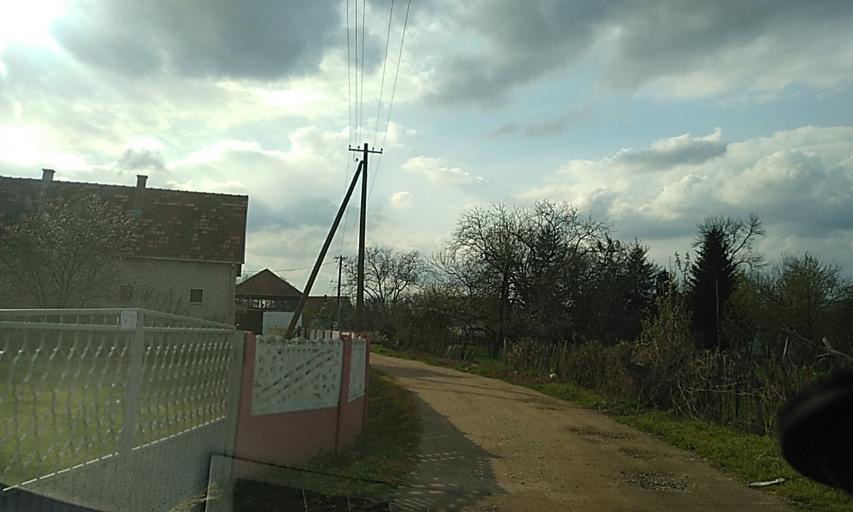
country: RS
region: Central Serbia
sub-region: Nisavski Okrug
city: Razanj
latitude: 43.5933
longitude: 21.6095
